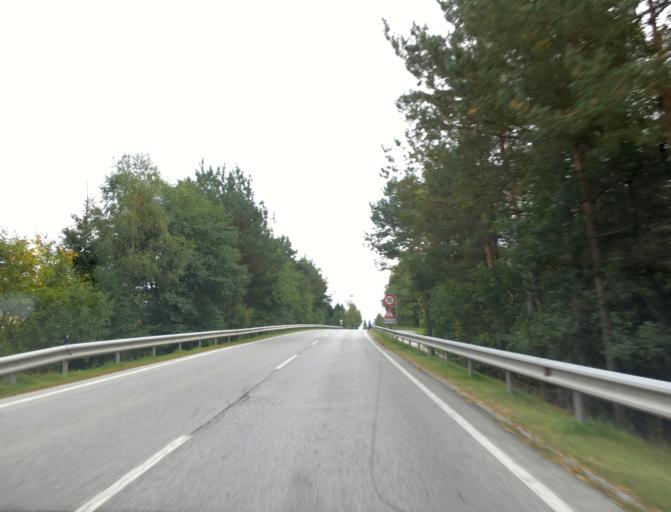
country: AT
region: Lower Austria
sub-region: Politischer Bezirk Neunkirchen
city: Thomasberg
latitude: 47.5427
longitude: 16.1532
